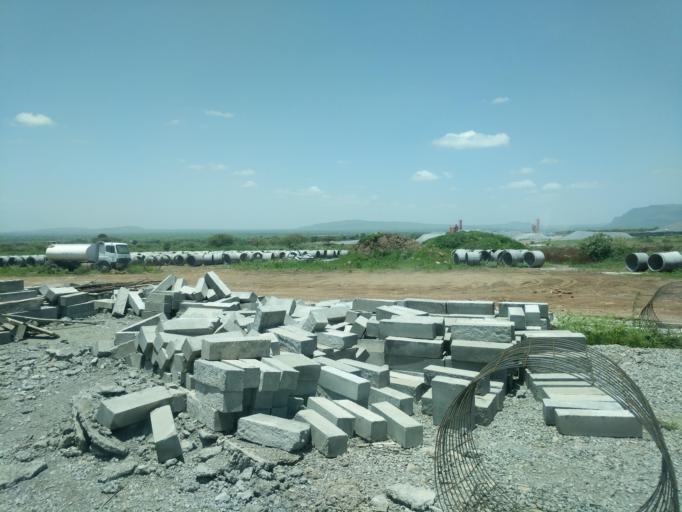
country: ET
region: Oromiya
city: Ziway
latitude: 7.9352
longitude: 38.6198
